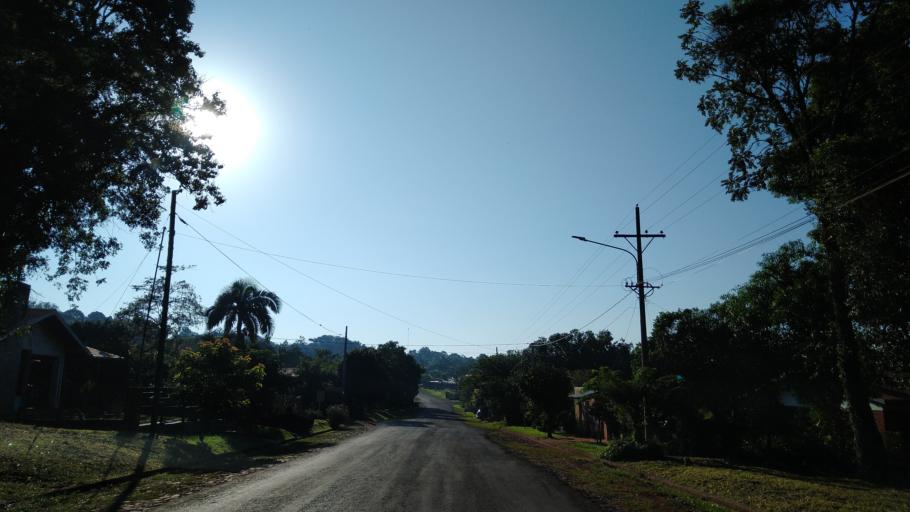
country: AR
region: Misiones
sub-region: Departamento de Montecarlo
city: Montecarlo
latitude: -26.5694
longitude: -54.7724
